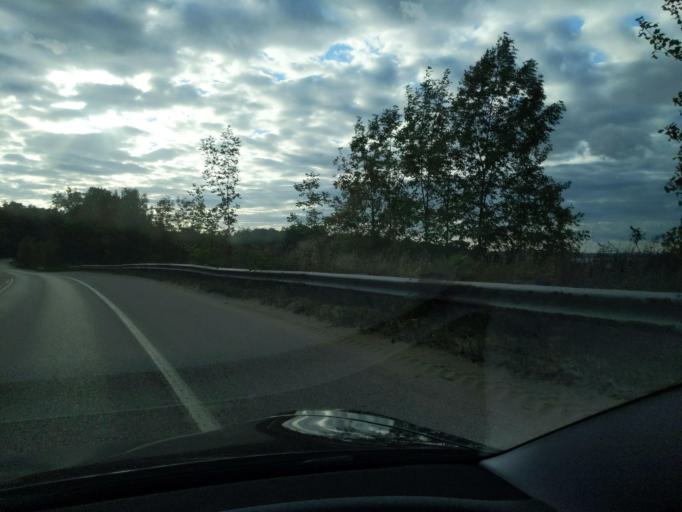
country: US
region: Michigan
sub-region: Kalkaska County
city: Rapid City
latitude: 44.7815
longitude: -85.2862
